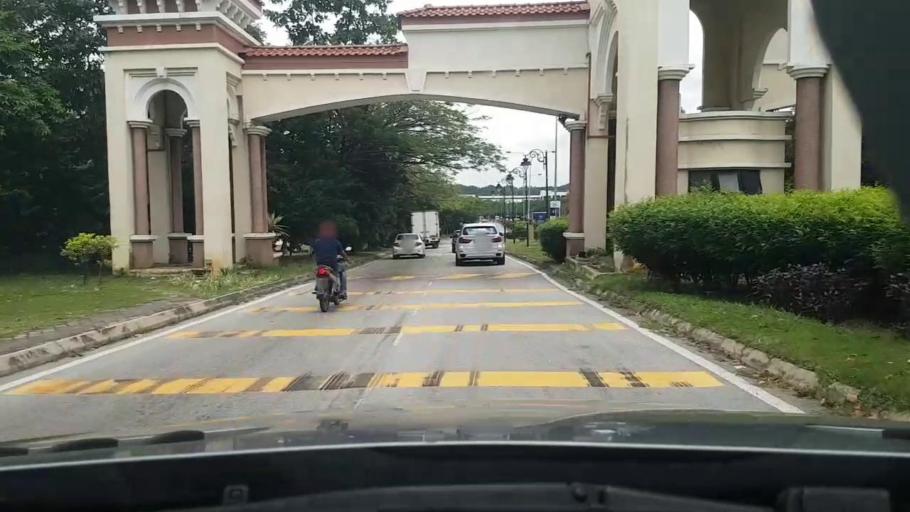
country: MY
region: Putrajaya
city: Putrajaya
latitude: 2.9800
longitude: 101.6290
